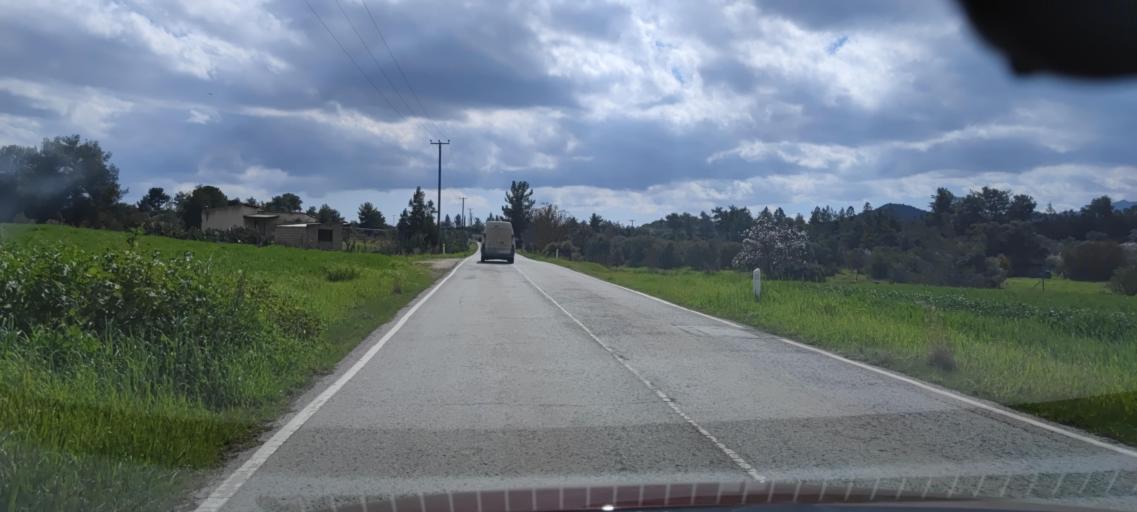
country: CY
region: Lefkosia
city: Lythrodontas
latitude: 34.9843
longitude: 33.2963
